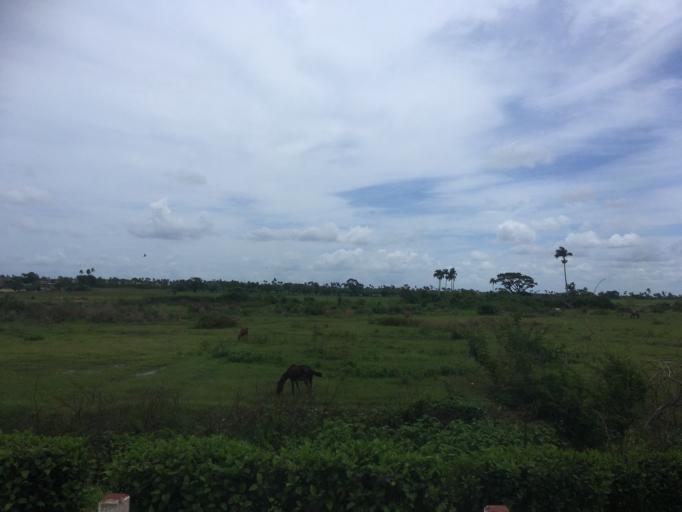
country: CU
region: Matanzas
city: Colon
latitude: 22.7126
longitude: -80.8961
